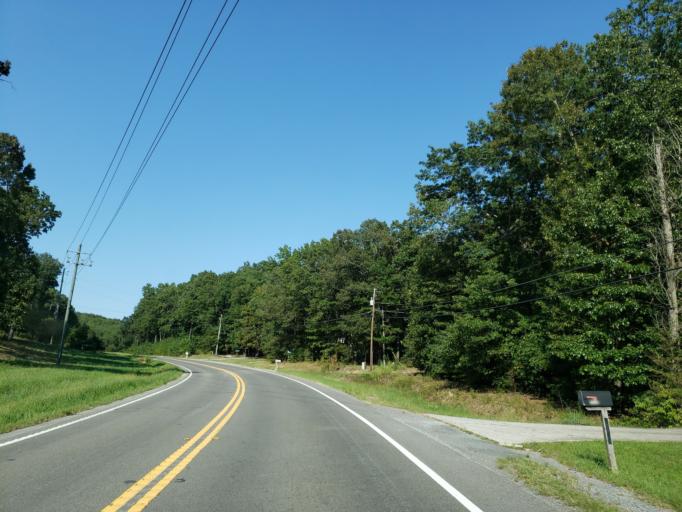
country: US
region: Georgia
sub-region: Whitfield County
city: Varnell
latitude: 34.8971
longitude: -85.0338
